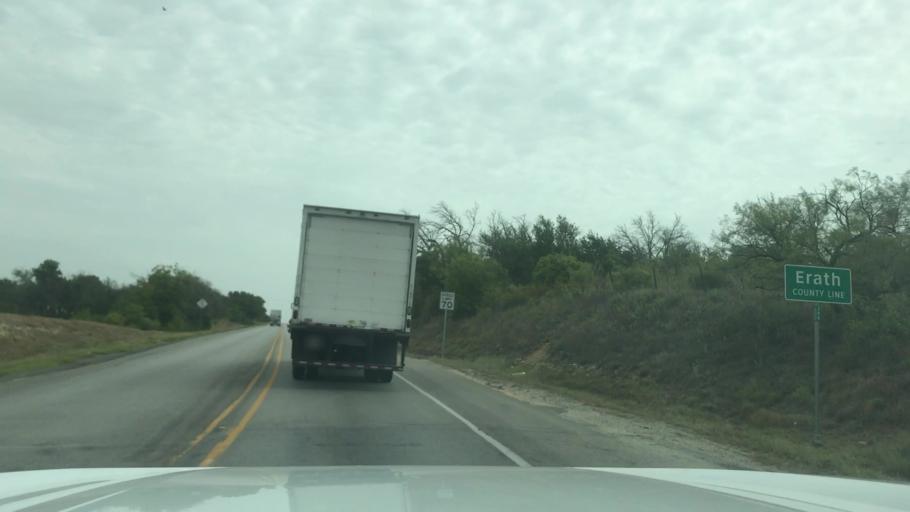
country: US
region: Texas
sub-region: Erath County
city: Dublin
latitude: 32.0877
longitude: -98.4295
